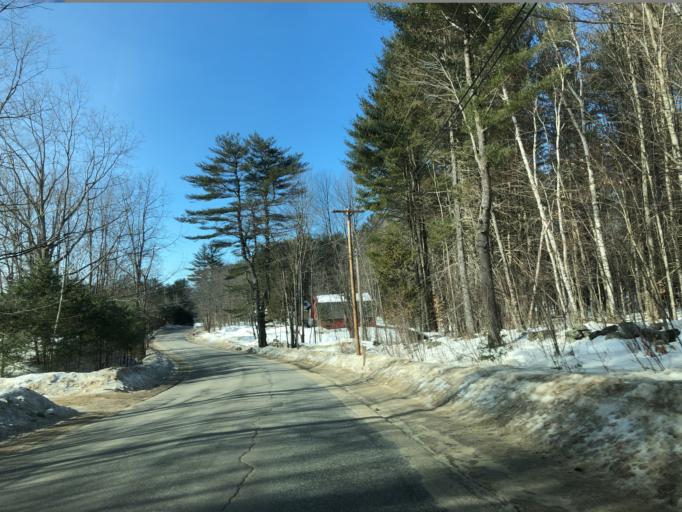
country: US
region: Maine
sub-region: Oxford County
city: Buckfield
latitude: 44.2963
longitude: -70.3728
